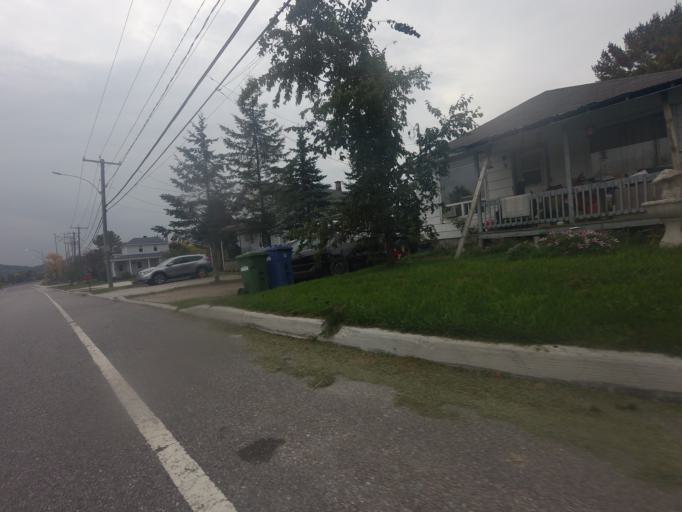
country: CA
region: Quebec
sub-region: Outaouais
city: Maniwaki
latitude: 46.0909
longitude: -76.0504
